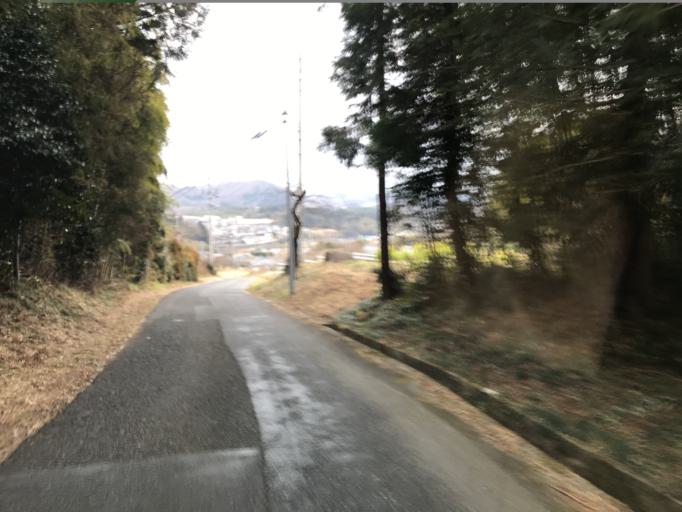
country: JP
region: Fukushima
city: Iwaki
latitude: 37.0537
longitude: 140.7907
